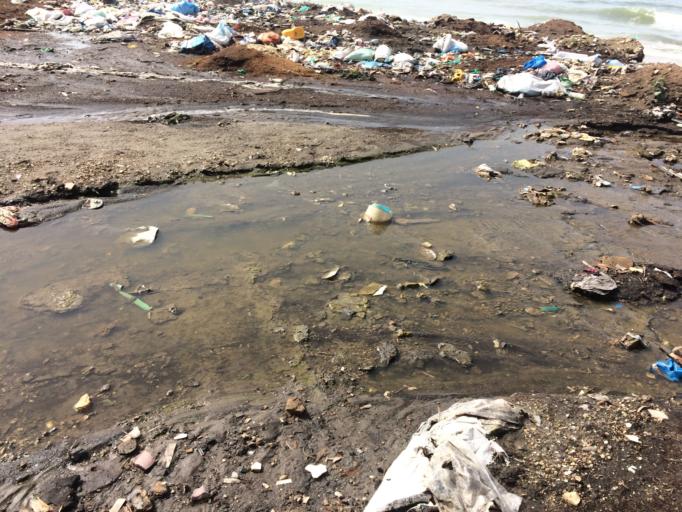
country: SN
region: Dakar
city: Pikine
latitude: 14.7261
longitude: -17.3182
